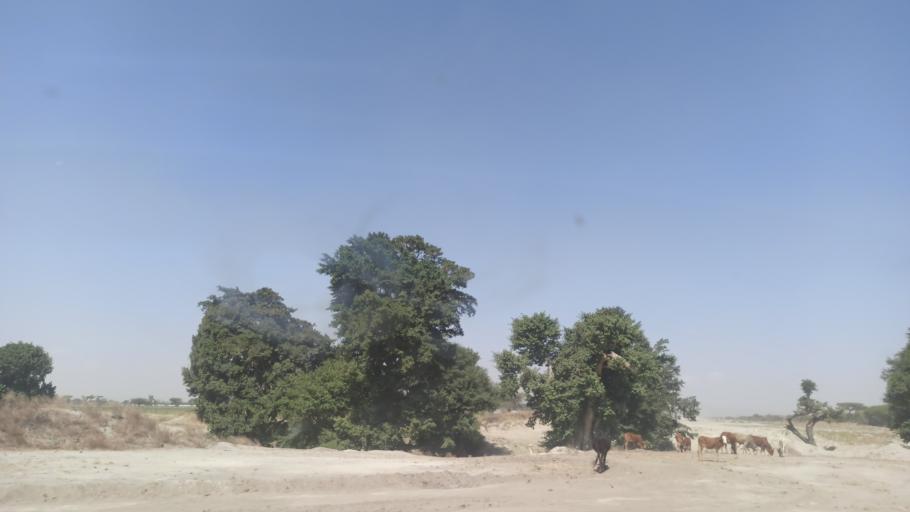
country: ET
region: Oromiya
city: Ziway
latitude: 7.7038
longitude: 38.6396
